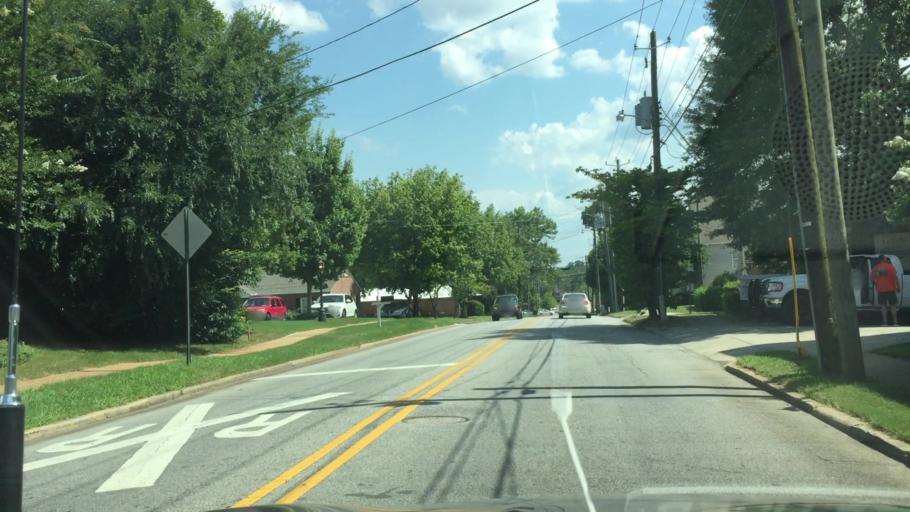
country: US
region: Alabama
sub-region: Lee County
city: Auburn
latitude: 32.6115
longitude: -85.4754
